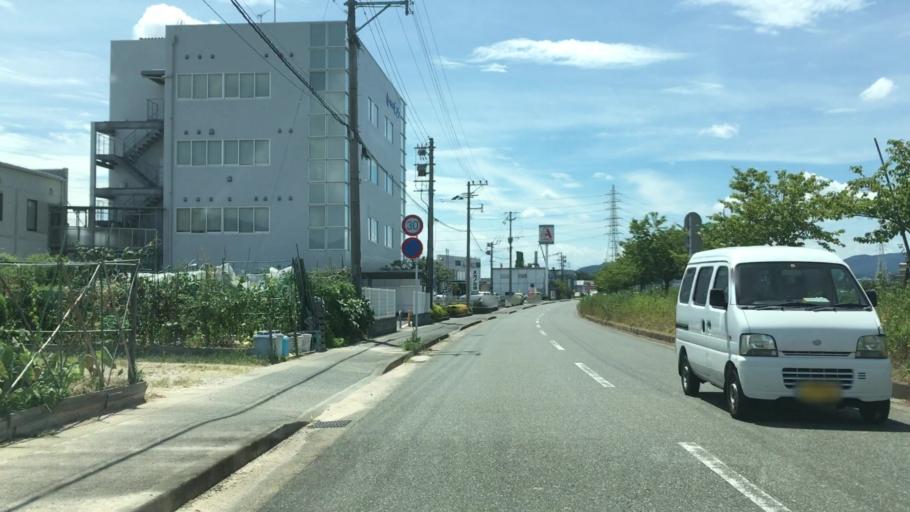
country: JP
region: Fukuoka
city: Onojo
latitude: 33.5424
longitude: 130.4827
